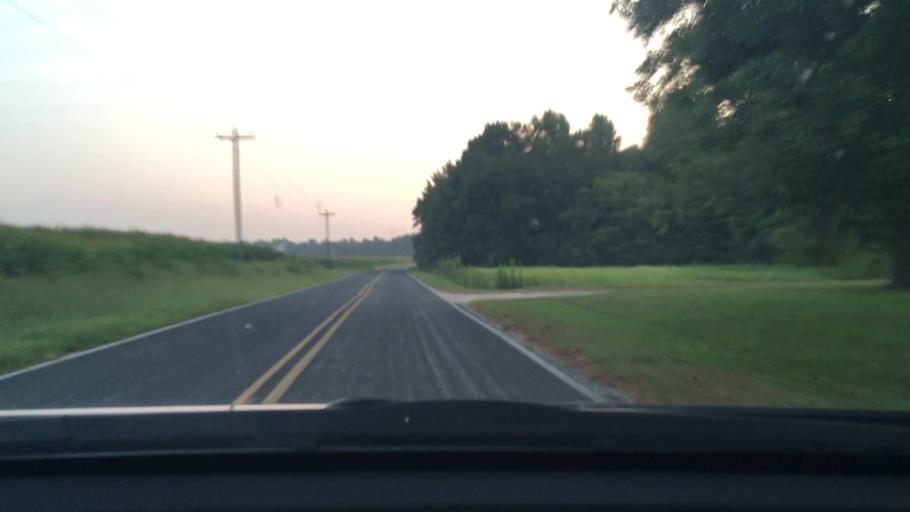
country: US
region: South Carolina
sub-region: Lee County
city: Bishopville
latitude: 34.1801
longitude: -80.1434
